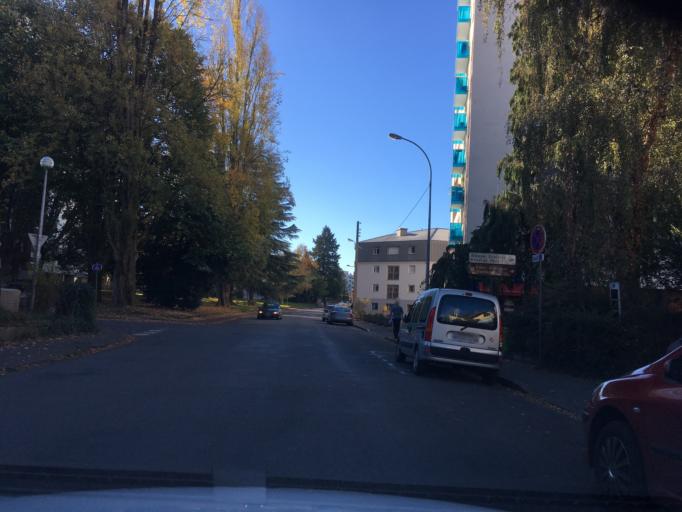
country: FR
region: Aquitaine
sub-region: Departement des Pyrenees-Atlantiques
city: Pau
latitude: 43.3068
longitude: -0.3566
